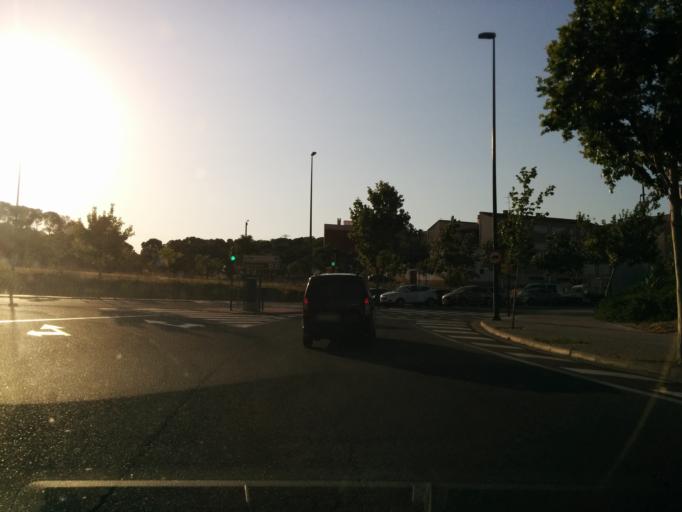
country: ES
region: Aragon
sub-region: Provincia de Zaragoza
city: Zaragoza
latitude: 41.6211
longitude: -0.8758
